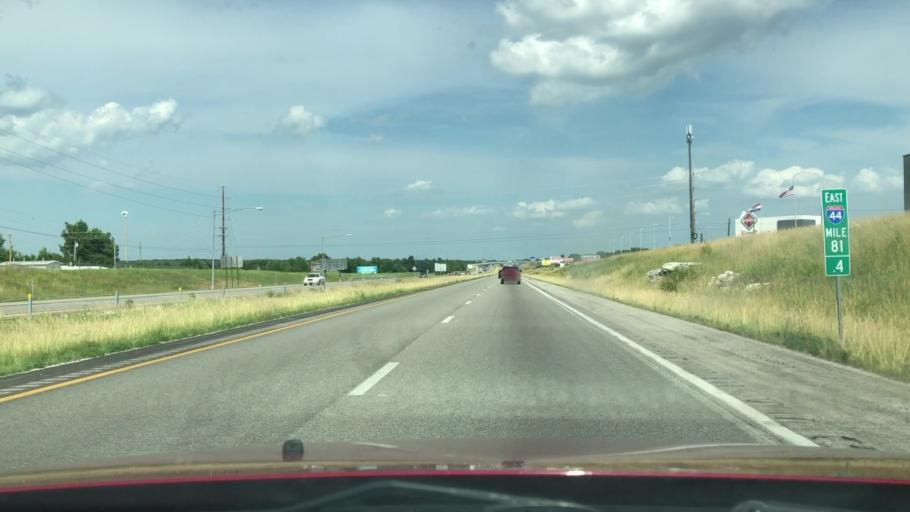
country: US
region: Missouri
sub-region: Greene County
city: Springfield
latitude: 37.2502
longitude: -93.2447
